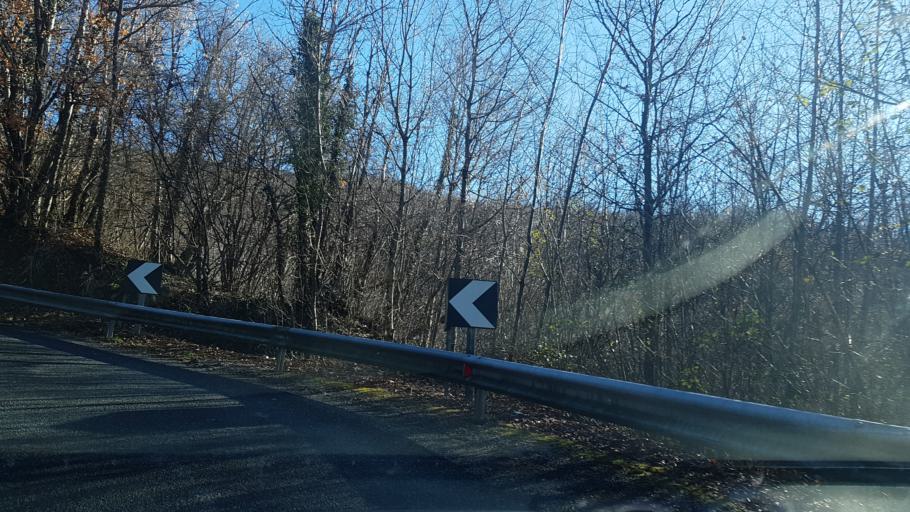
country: IT
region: Friuli Venezia Giulia
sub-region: Provincia di Udine
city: Montenars
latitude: 46.2485
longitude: 13.1601
